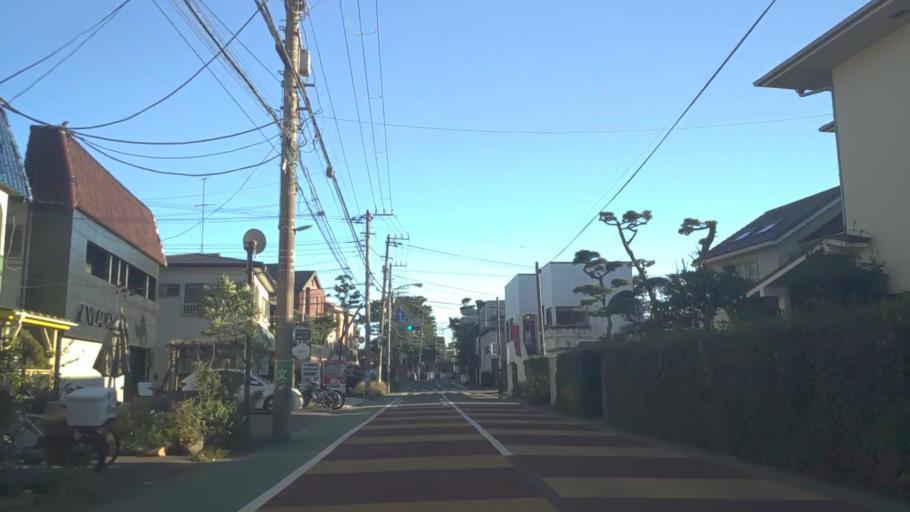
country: JP
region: Kanagawa
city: Chigasaki
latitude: 35.3231
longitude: 139.4152
